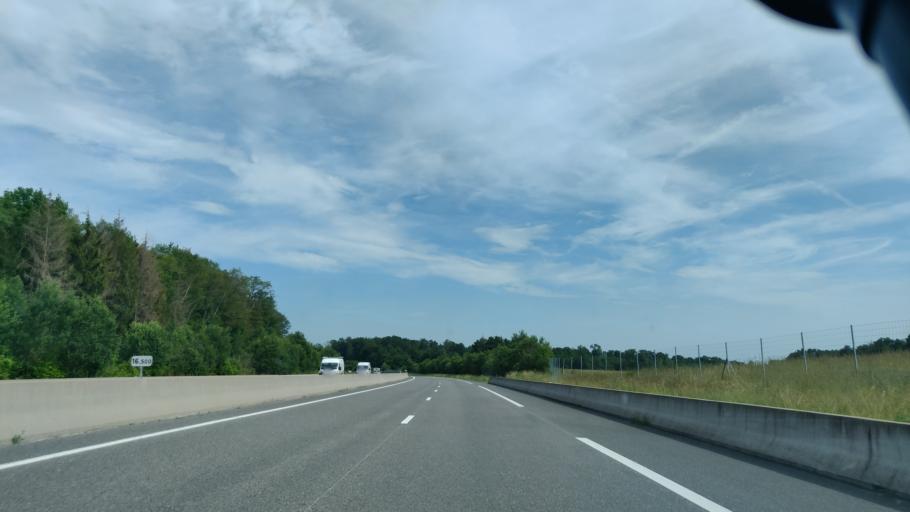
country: FR
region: Lorraine
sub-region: Departement de Meurthe-et-Moselle
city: Baccarat
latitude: 48.5071
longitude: 6.6720
